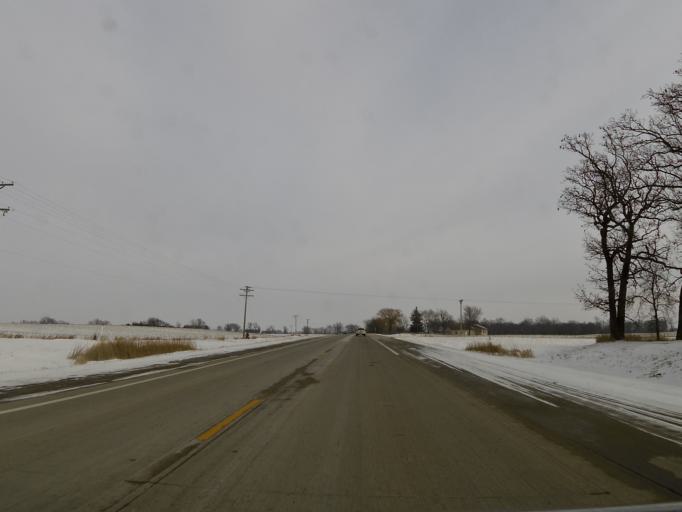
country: US
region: Minnesota
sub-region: McLeod County
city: Hutchinson
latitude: 44.8926
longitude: -94.2340
